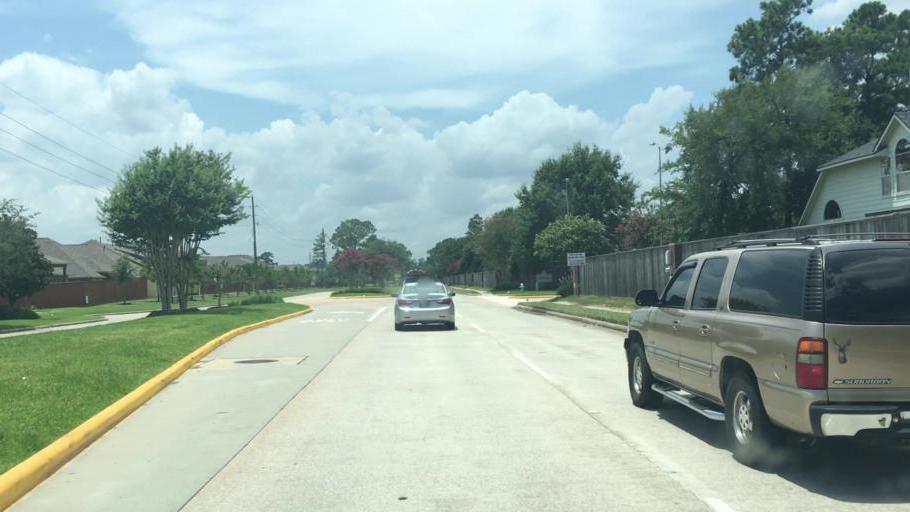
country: US
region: Texas
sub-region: Harris County
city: Atascocita
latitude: 29.9780
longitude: -95.2056
